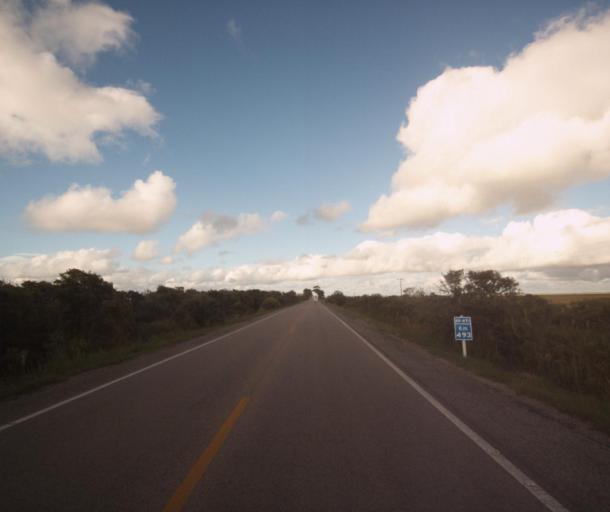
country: BR
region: Rio Grande do Sul
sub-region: Rio Grande
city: Rio Grande
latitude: -32.1920
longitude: -52.4350
